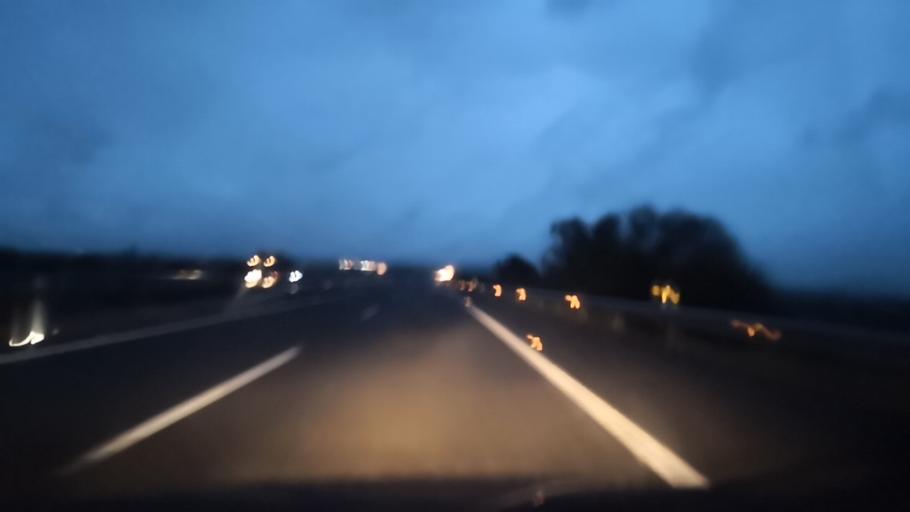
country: ES
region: Extremadura
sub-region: Provincia de Caceres
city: Aldea del Cano
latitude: 39.3633
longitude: -6.3394
